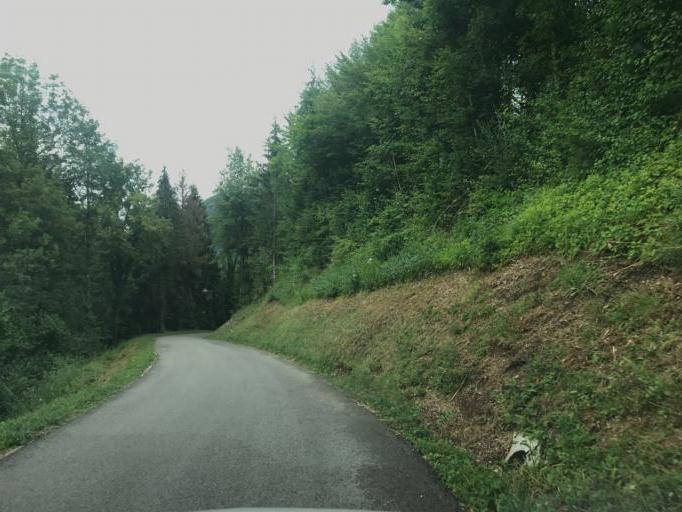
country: FR
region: Franche-Comte
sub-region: Departement du Jura
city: Saint-Claude
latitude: 46.3668
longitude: 5.8695
